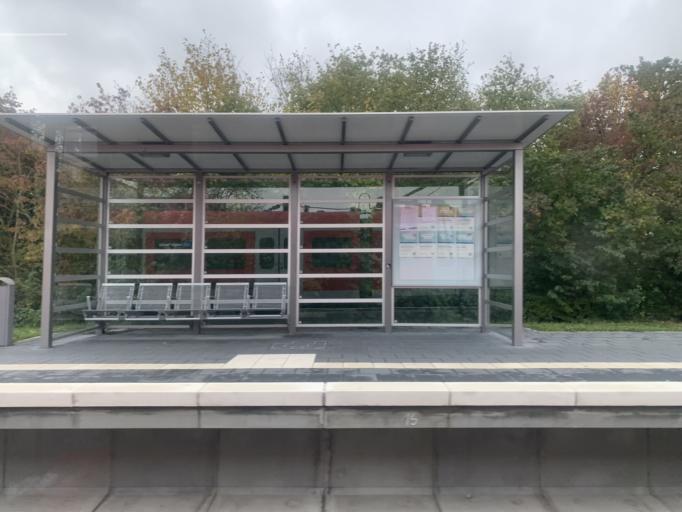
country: DE
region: Bavaria
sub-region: Upper Bavaria
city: Unterschleissheim
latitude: 48.2742
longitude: 11.5690
